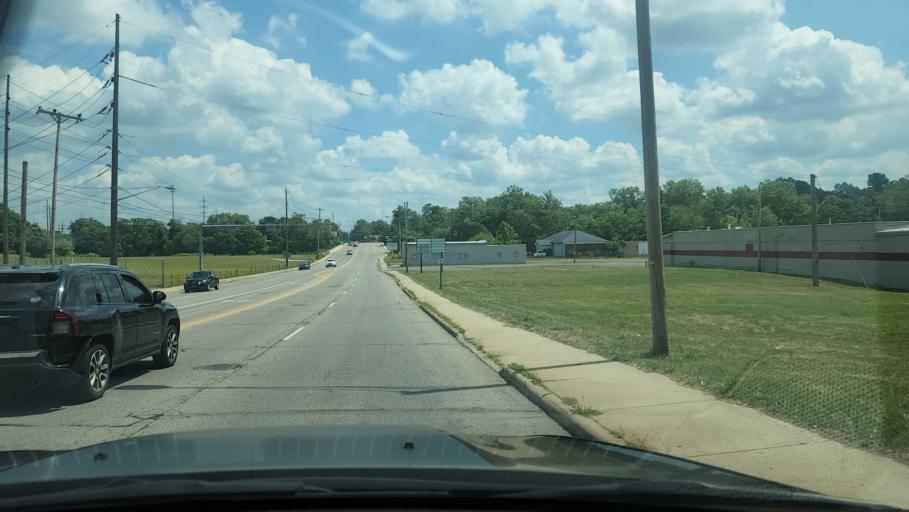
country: US
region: Ohio
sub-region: Trumbull County
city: Warren
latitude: 41.2427
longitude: -80.8304
